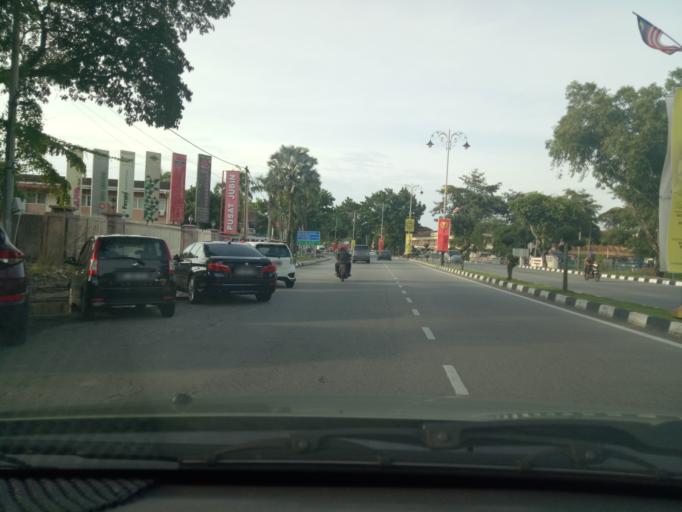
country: MY
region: Kedah
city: Alor Setar
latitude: 6.1397
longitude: 100.3704
